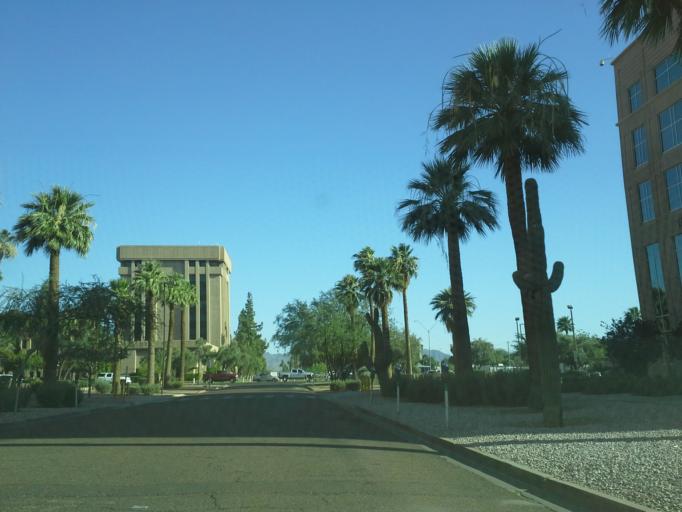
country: US
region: Arizona
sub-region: Maricopa County
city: Phoenix
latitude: 33.4502
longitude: -112.0982
